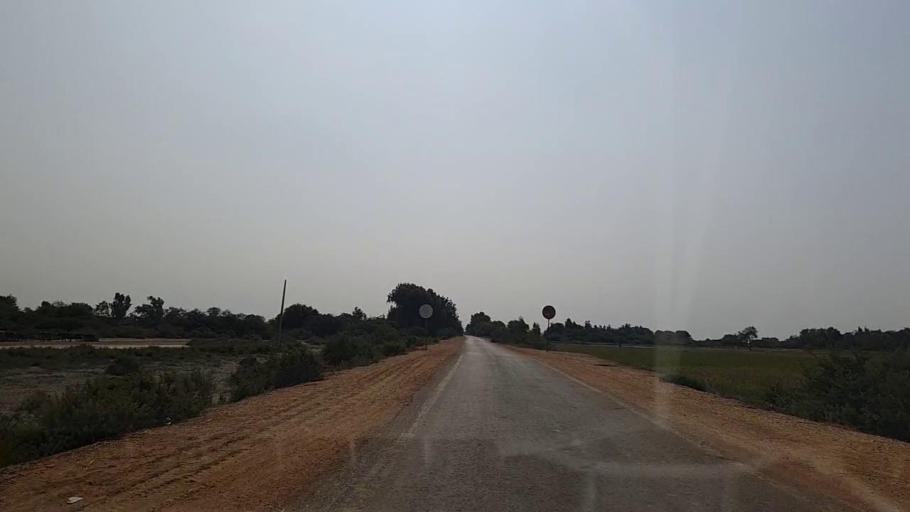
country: PK
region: Sindh
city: Chuhar Jamali
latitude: 24.2481
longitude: 67.9050
